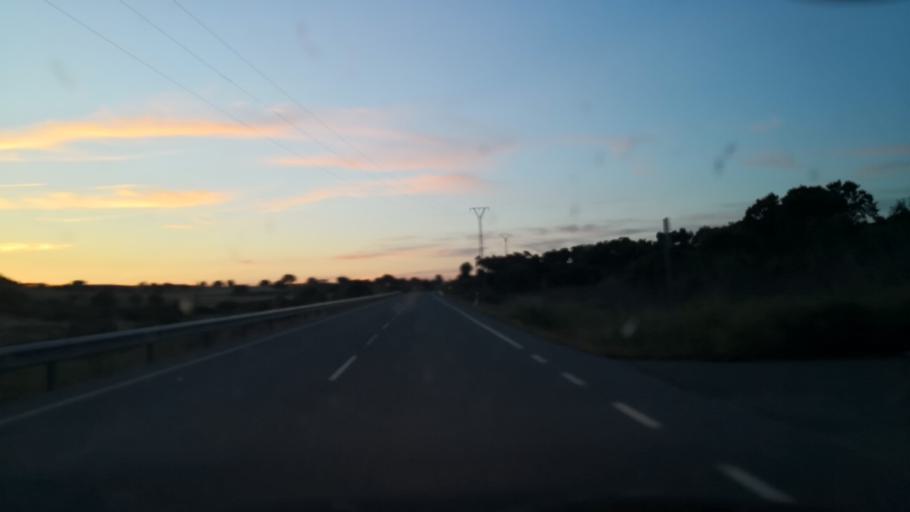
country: ES
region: Extremadura
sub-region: Provincia de Caceres
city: Piedras Albas
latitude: 39.7707
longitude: -6.9150
